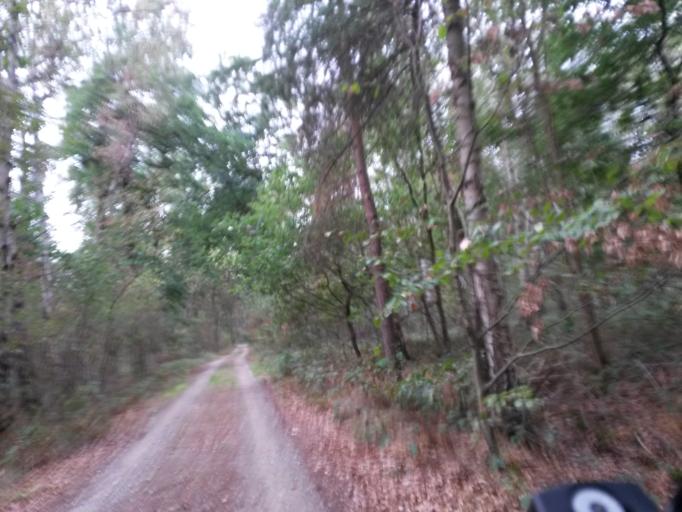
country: DE
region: Saxony-Anhalt
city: Tangerhutte
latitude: 52.4939
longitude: 11.8888
